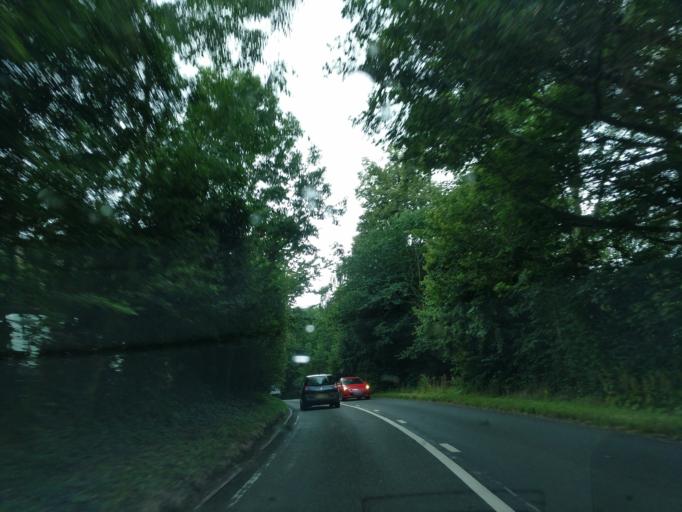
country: GB
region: England
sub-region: Staffordshire
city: Colwich
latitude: 52.7891
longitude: -2.0149
